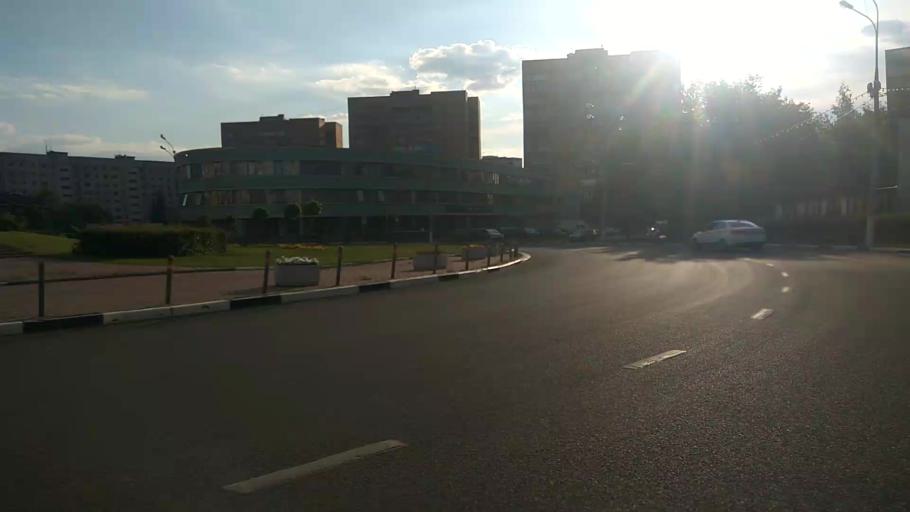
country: RU
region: Moskovskaya
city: Mytishchi
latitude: 55.9037
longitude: 37.7154
